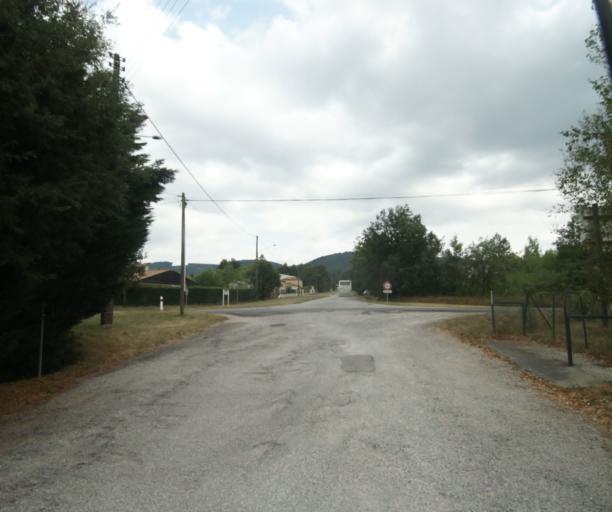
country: FR
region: Midi-Pyrenees
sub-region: Departement de la Haute-Garonne
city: Revel
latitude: 43.4340
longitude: 2.0151
